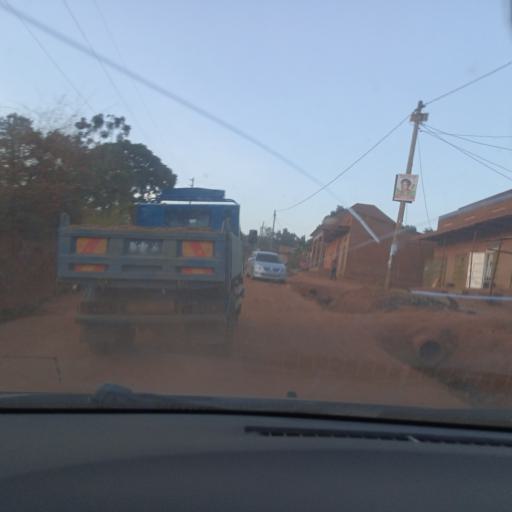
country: UG
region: Central Region
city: Masaka
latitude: -0.3177
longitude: 31.7689
